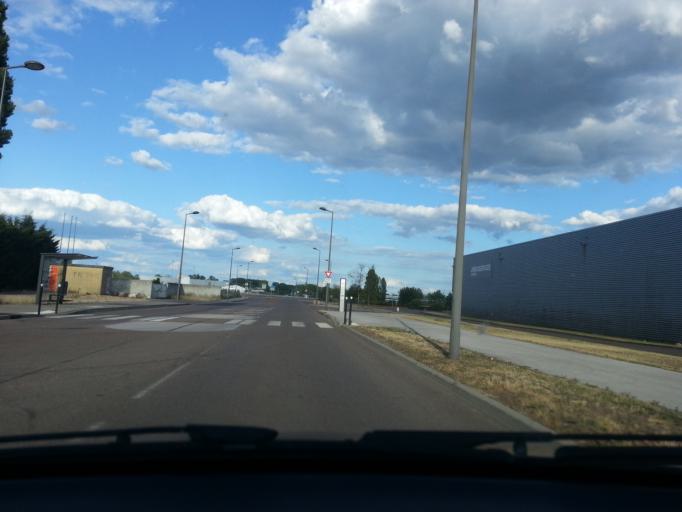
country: FR
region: Bourgogne
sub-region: Departement de Saone-et-Loire
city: Chalon-sur-Saone
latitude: 46.7684
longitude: 4.8682
